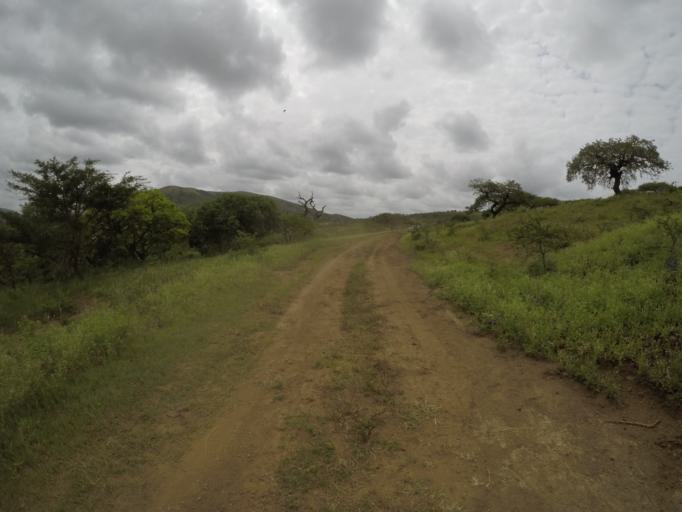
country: ZA
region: KwaZulu-Natal
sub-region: uThungulu District Municipality
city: Empangeni
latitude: -28.6156
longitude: 31.8891
